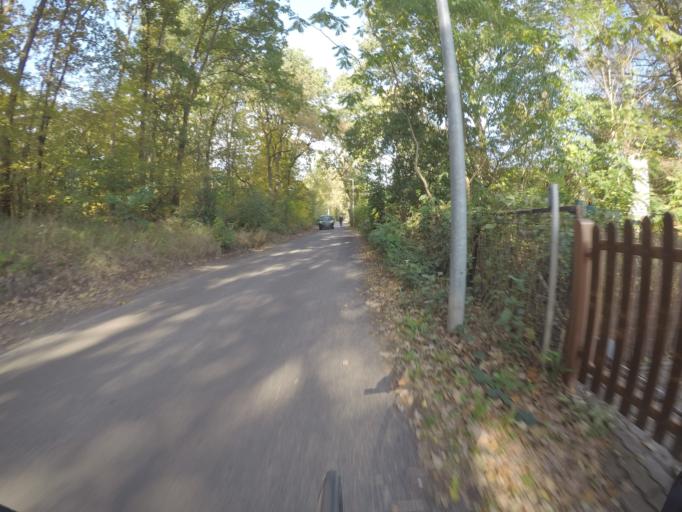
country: DE
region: Brandenburg
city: Oranienburg
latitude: 52.7326
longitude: 13.2279
